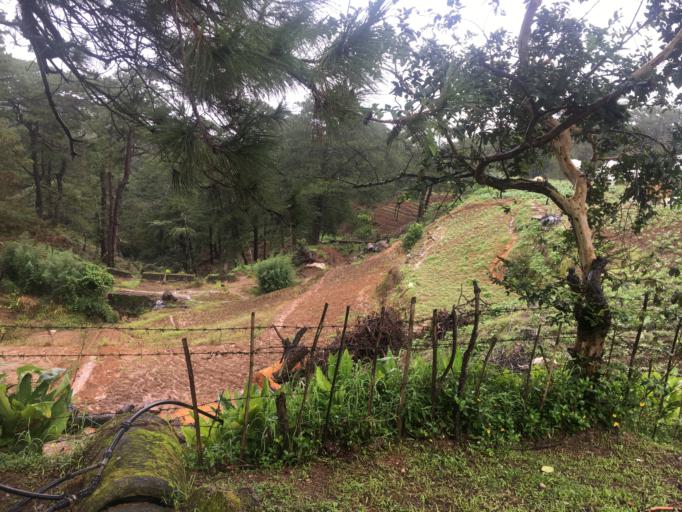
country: PH
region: Cordillera
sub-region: Province of Benguet
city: Tuding
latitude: 16.3708
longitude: 120.6242
